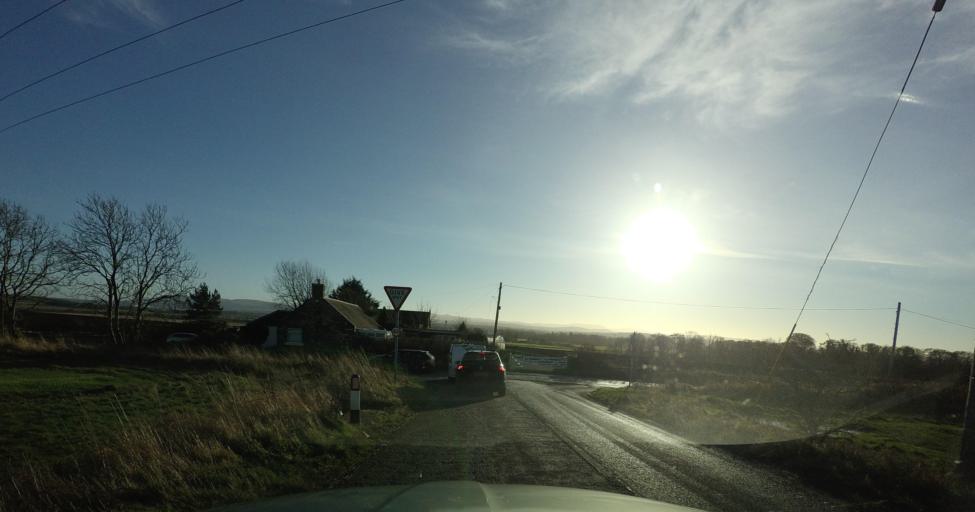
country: GB
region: Scotland
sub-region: Edinburgh
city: Kirkliston
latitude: 55.9665
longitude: -3.3735
